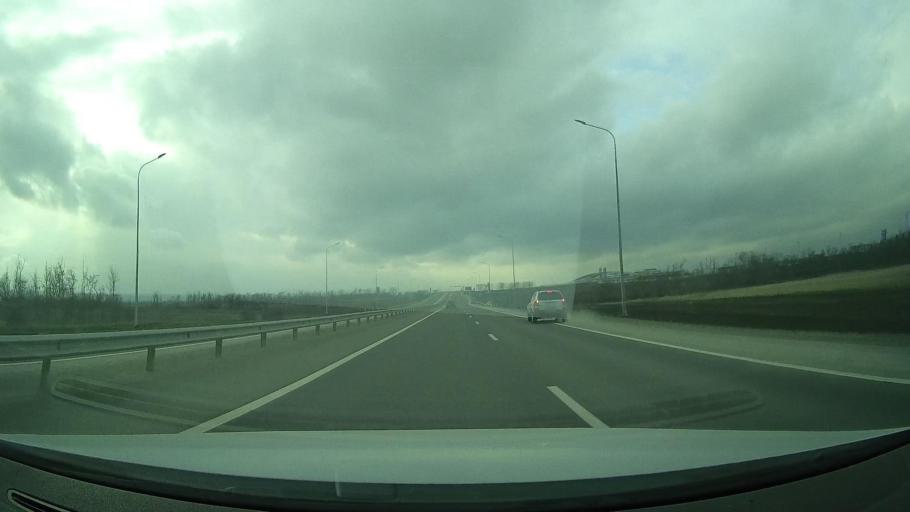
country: RU
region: Rostov
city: Grushevskaya
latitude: 47.4927
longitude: 39.9489
